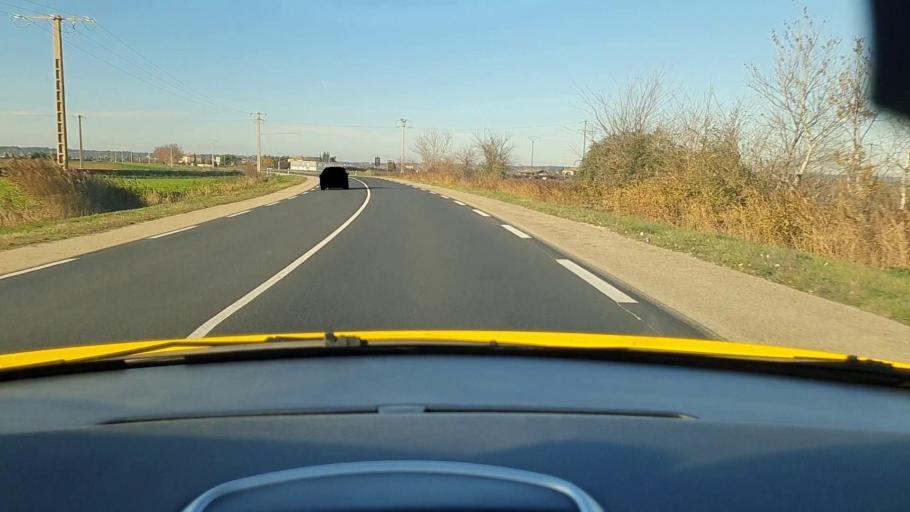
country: FR
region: Languedoc-Roussillon
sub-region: Departement du Gard
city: Bellegarde
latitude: 43.7215
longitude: 4.5474
